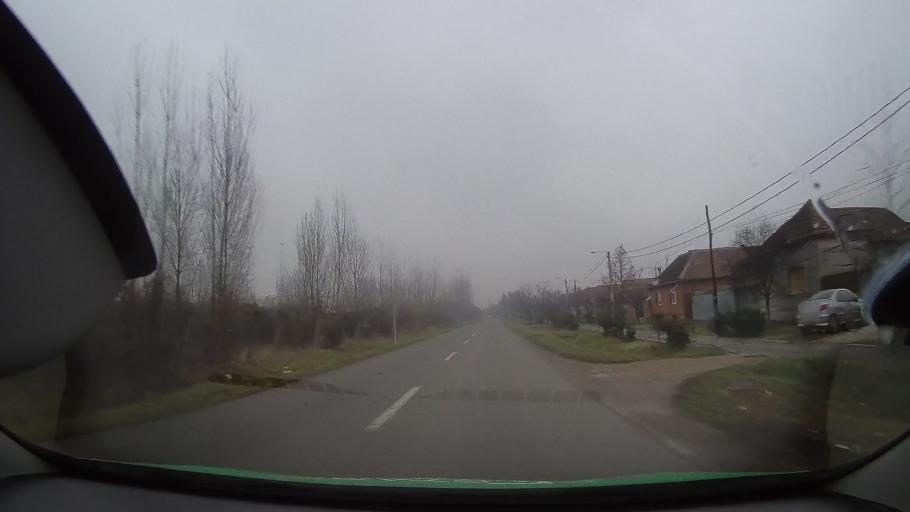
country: RO
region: Bihor
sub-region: Municipiul Salonta
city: Salonta
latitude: 46.8039
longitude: 21.6382
